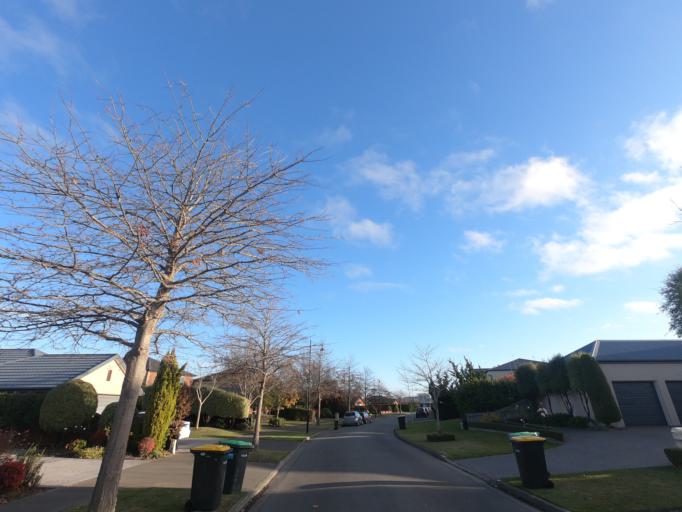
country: NZ
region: Canterbury
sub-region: Selwyn District
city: Prebbleton
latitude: -43.5658
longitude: 172.5714
